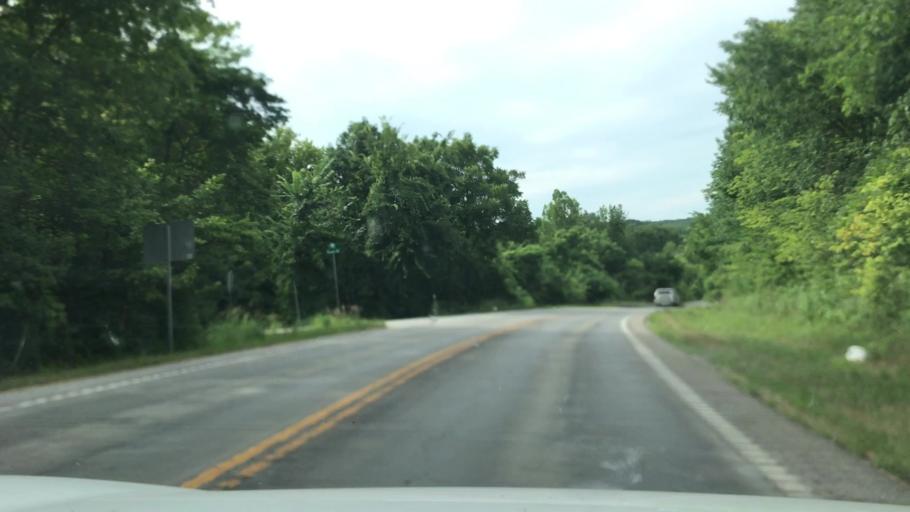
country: US
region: Missouri
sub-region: Saint Charles County
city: Weldon Spring
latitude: 38.6434
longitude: -90.7746
